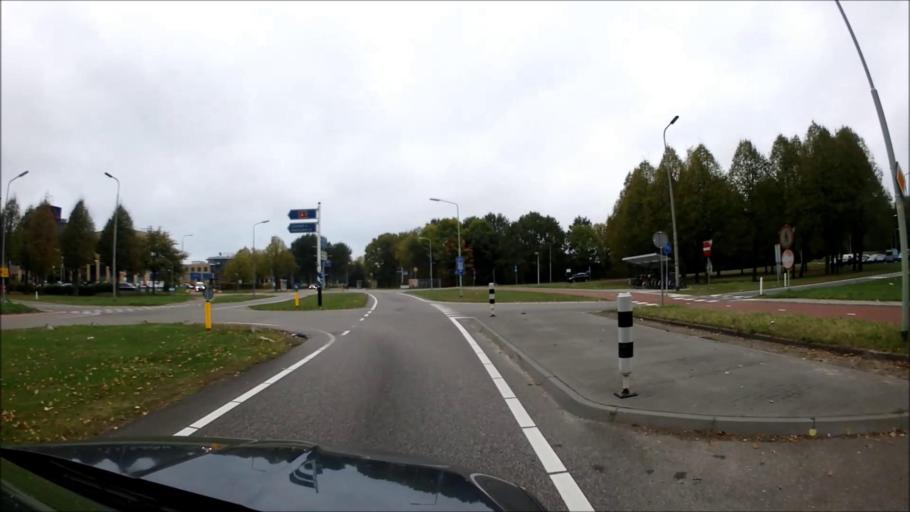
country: NL
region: North Holland
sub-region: Gemeente Naarden
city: Naarden
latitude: 52.3063
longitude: 5.1445
